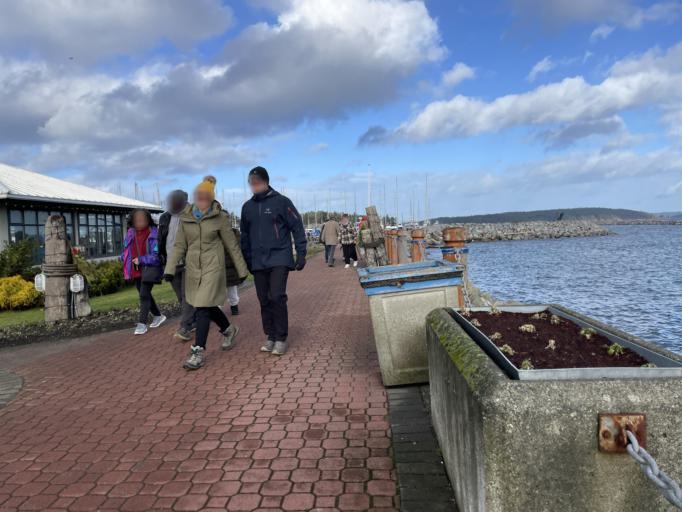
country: CA
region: British Columbia
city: North Saanich
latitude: 48.6506
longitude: -123.3938
